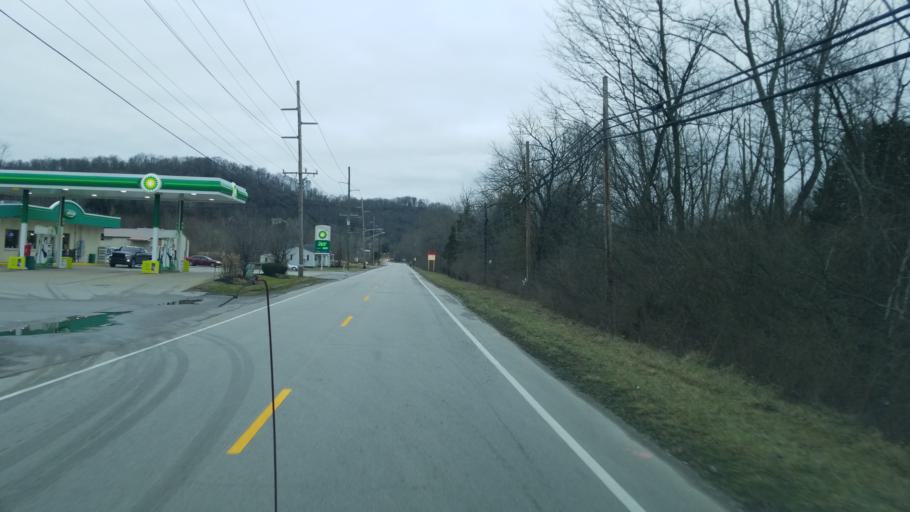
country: US
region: Kentucky
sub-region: Campbell County
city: Silver Grove
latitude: 39.0421
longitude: -84.4139
